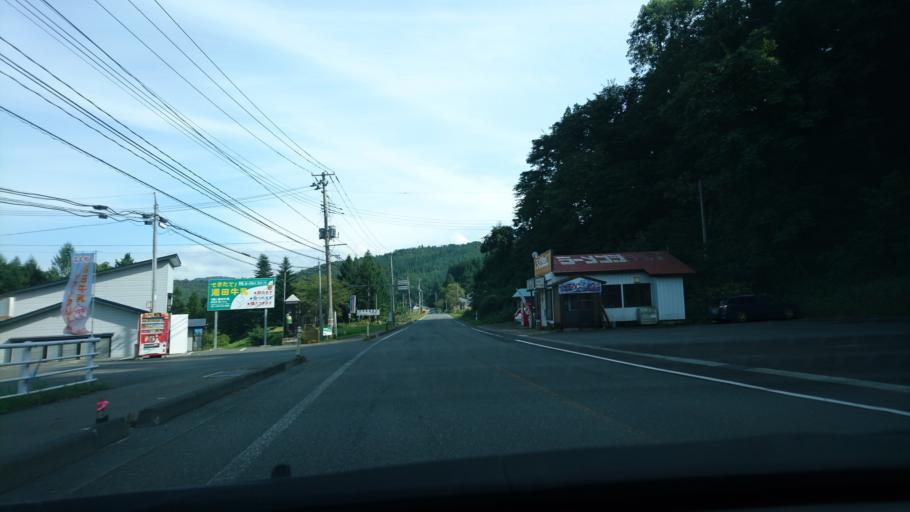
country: JP
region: Akita
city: Yokotemachi
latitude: 39.3139
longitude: 140.7571
